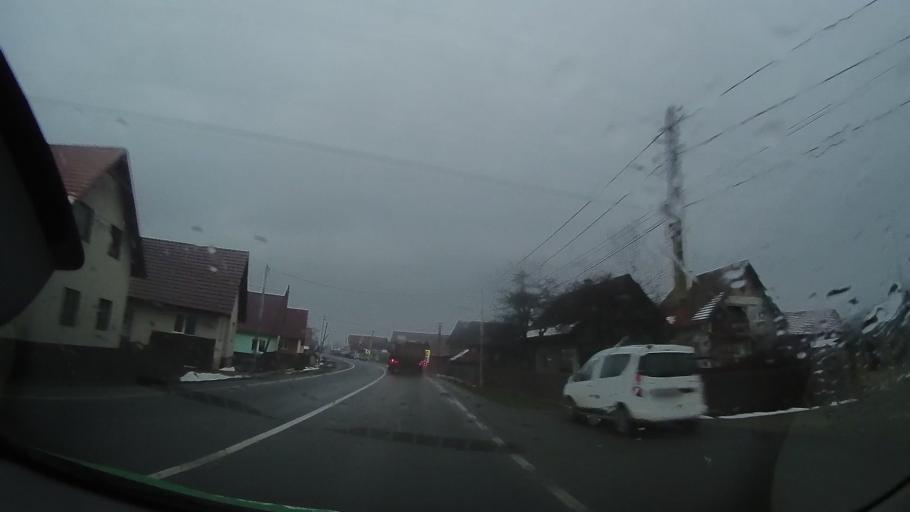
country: RO
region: Harghita
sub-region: Comuna Lazarea
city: Lazarea
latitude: 46.7555
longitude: 25.5189
